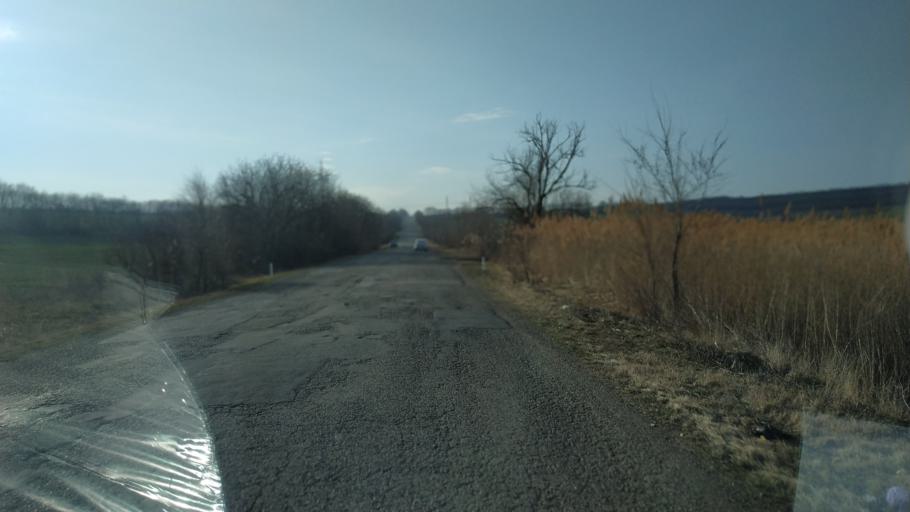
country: MD
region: Chisinau
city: Singera
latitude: 46.8805
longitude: 29.0393
